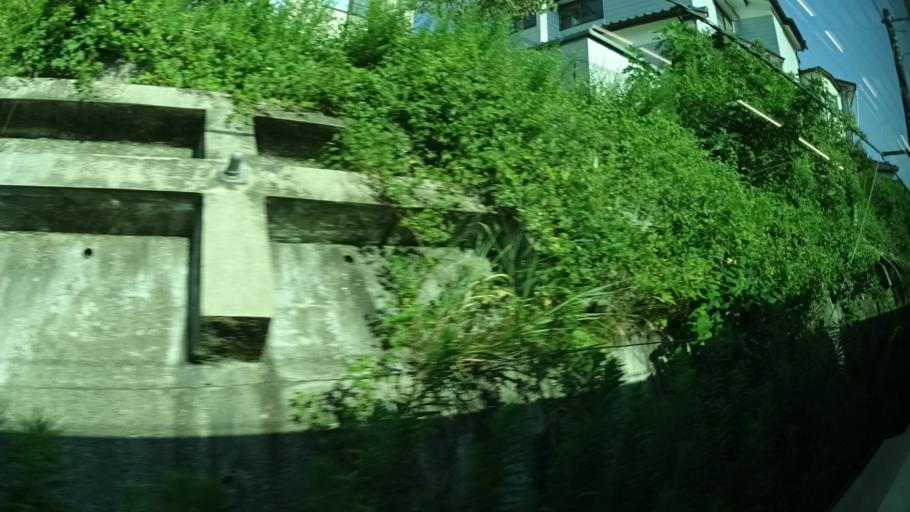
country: JP
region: Miyagi
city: Shiogama
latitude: 38.3128
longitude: 141.0097
